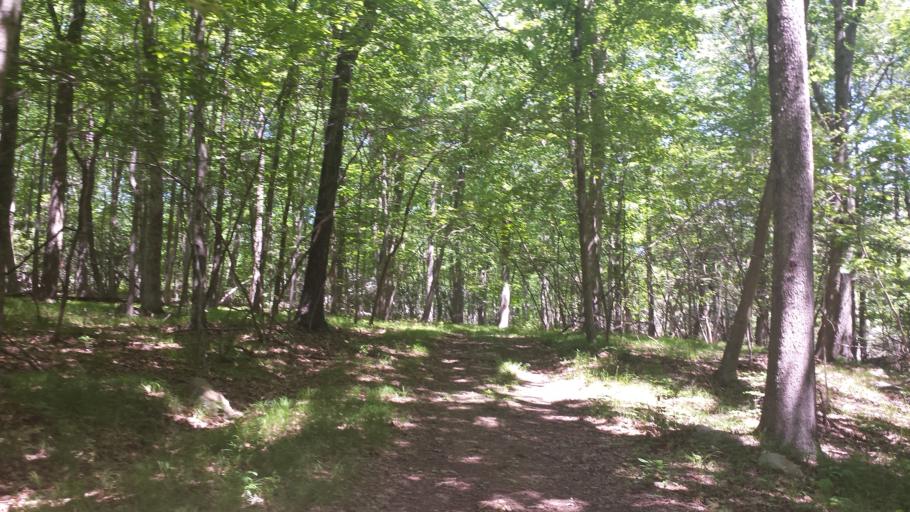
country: US
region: New York
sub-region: Westchester County
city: Pound Ridge
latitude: 41.2347
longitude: -73.5768
